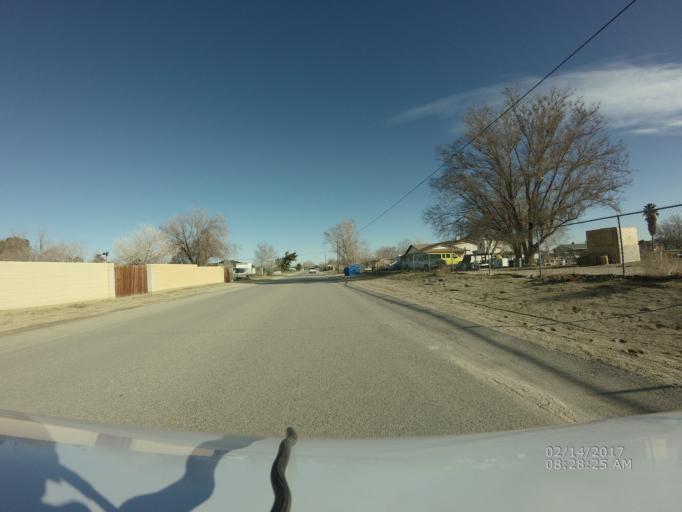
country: US
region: California
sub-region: Los Angeles County
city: Littlerock
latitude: 34.5550
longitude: -117.9494
